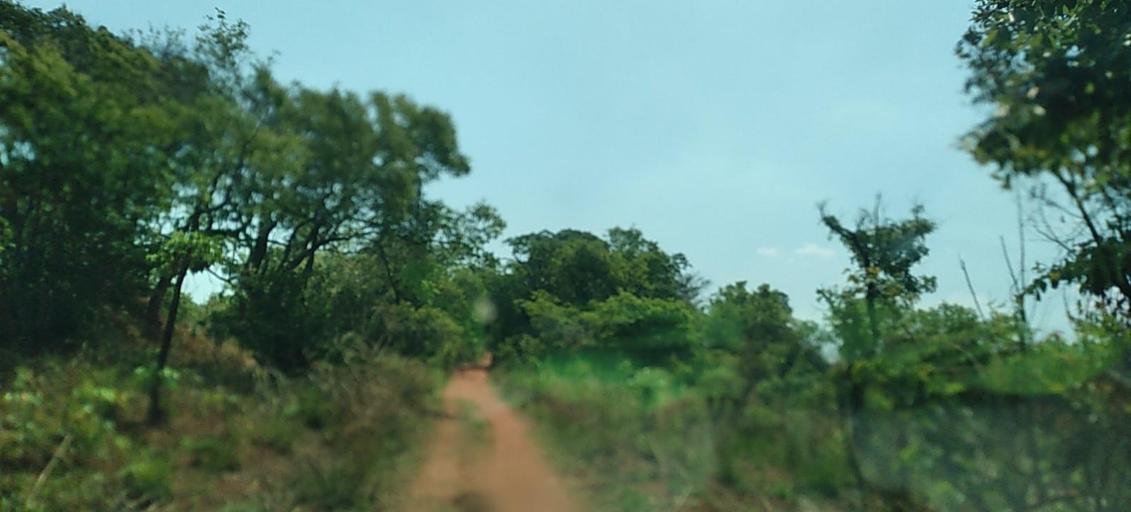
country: CD
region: Katanga
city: Kolwezi
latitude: -11.2821
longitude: 25.1424
